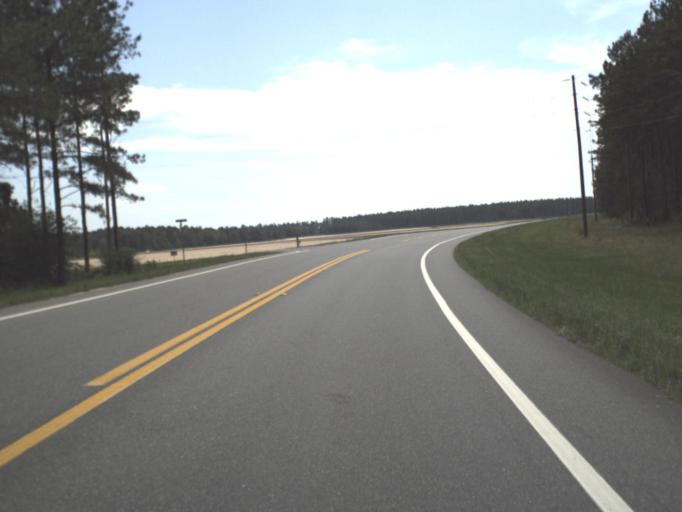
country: US
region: Florida
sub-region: Gulf County
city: Wewahitchka
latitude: 30.2277
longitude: -85.2048
